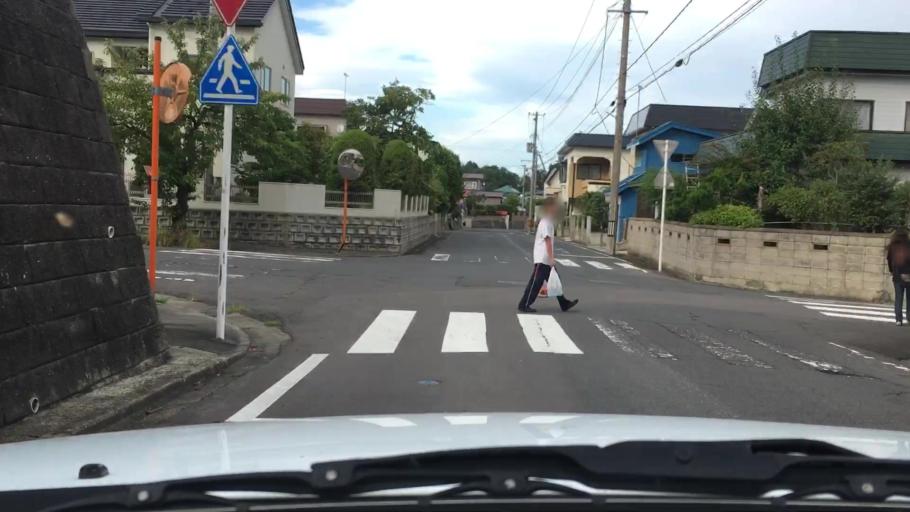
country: JP
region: Aomori
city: Hirosaki
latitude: 40.5746
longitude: 140.4534
